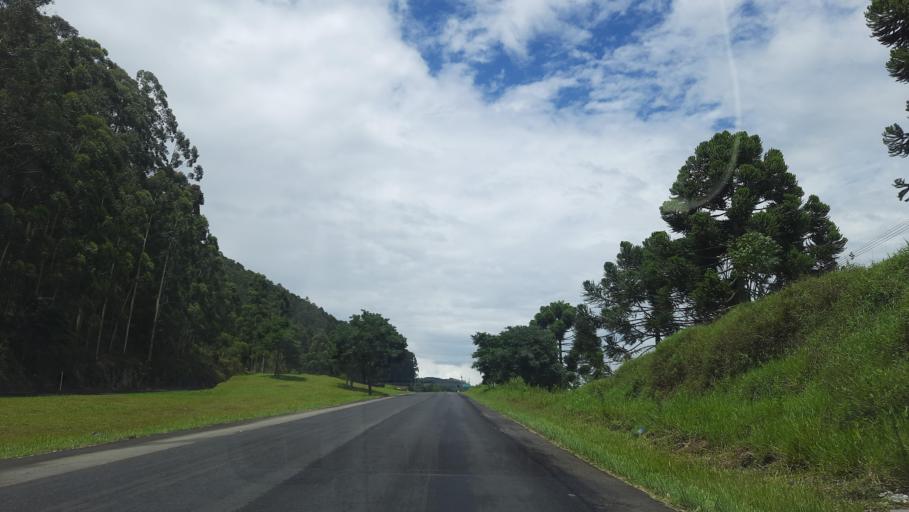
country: BR
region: Minas Gerais
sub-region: Pocos De Caldas
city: Pocos de Caldas
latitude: -21.8014
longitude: -46.6499
